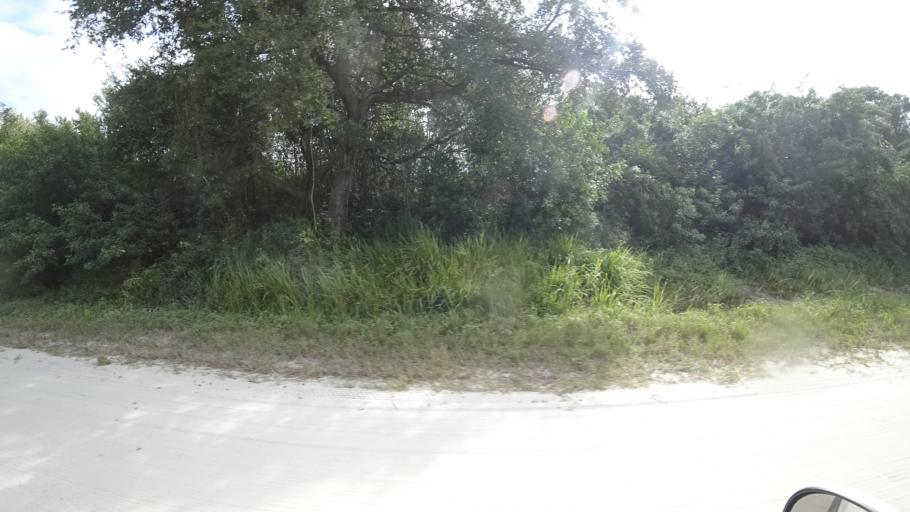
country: US
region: Florida
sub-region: Hillsborough County
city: Wimauma
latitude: 27.6008
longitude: -82.3119
